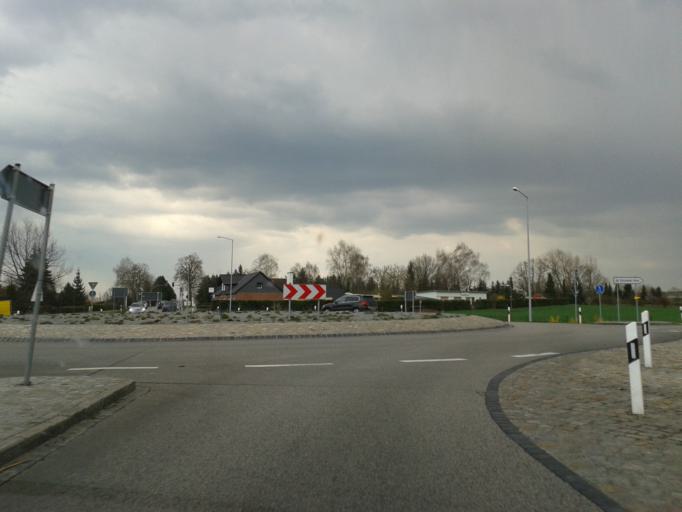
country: DE
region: Saxony-Anhalt
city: Salzwedel
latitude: 52.8614
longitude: 11.1165
